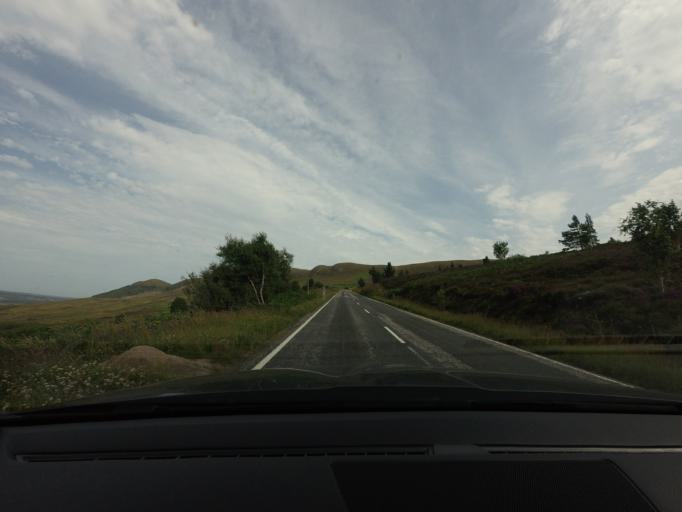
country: GB
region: Scotland
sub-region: Highland
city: Alness
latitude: 57.8419
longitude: -4.2757
